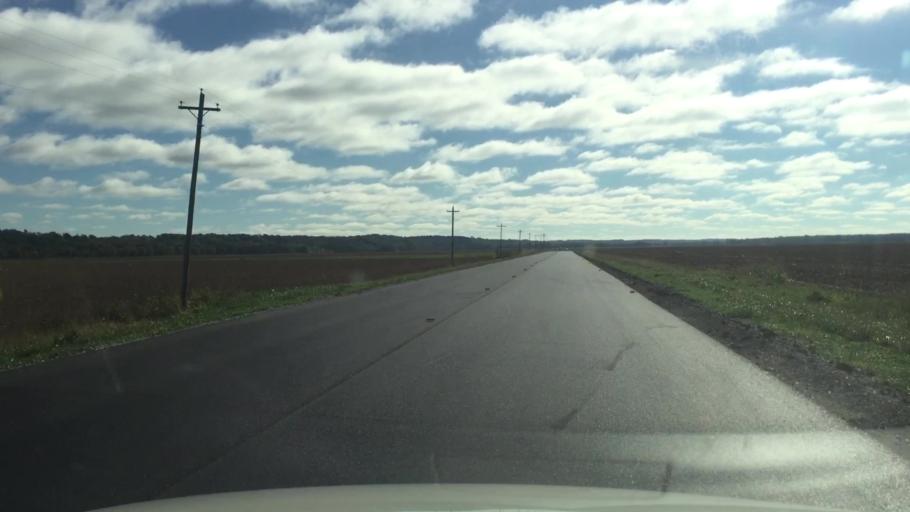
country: US
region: Missouri
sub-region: Howard County
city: New Franklin
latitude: 38.9943
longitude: -92.6554
